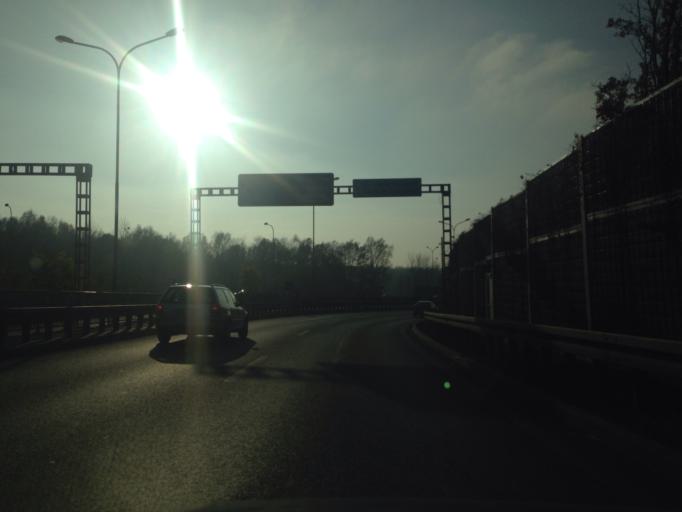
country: PL
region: Silesian Voivodeship
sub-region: Katowice
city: Katowice
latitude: 50.2431
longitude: 19.0497
